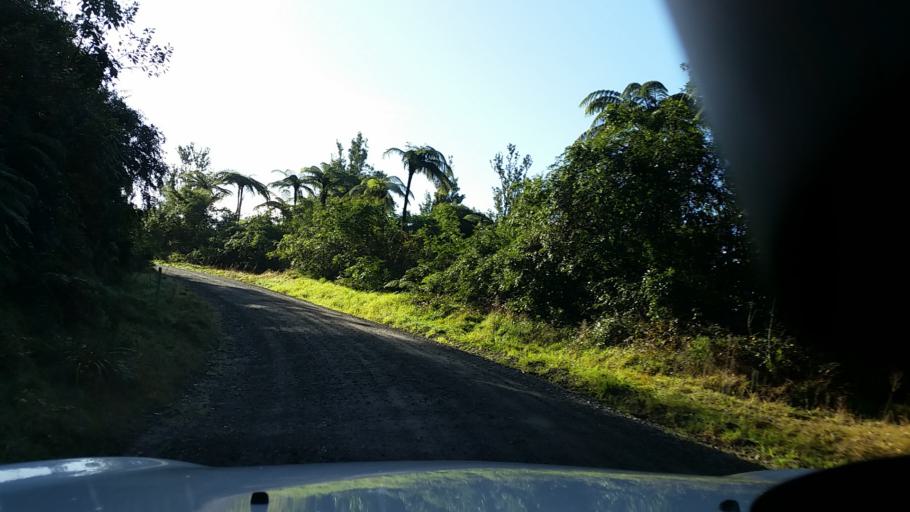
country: NZ
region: Bay of Plenty
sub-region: Kawerau District
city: Kawerau
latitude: -38.0282
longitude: 176.5582
